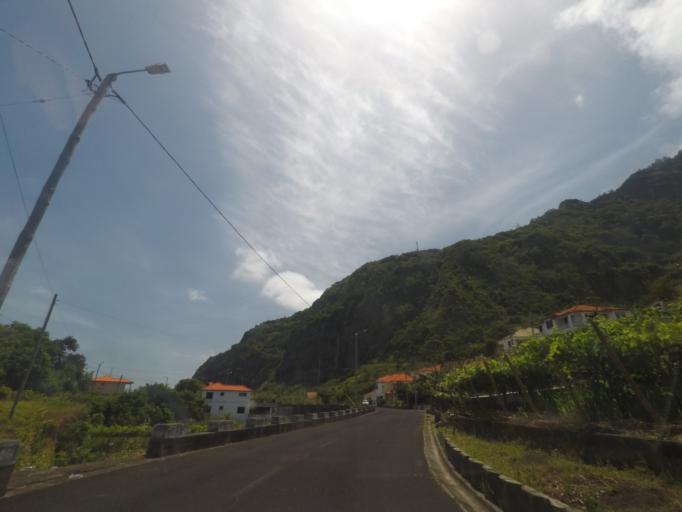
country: PT
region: Madeira
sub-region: Sao Vicente
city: Sao Vicente
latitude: 32.8264
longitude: -16.9897
